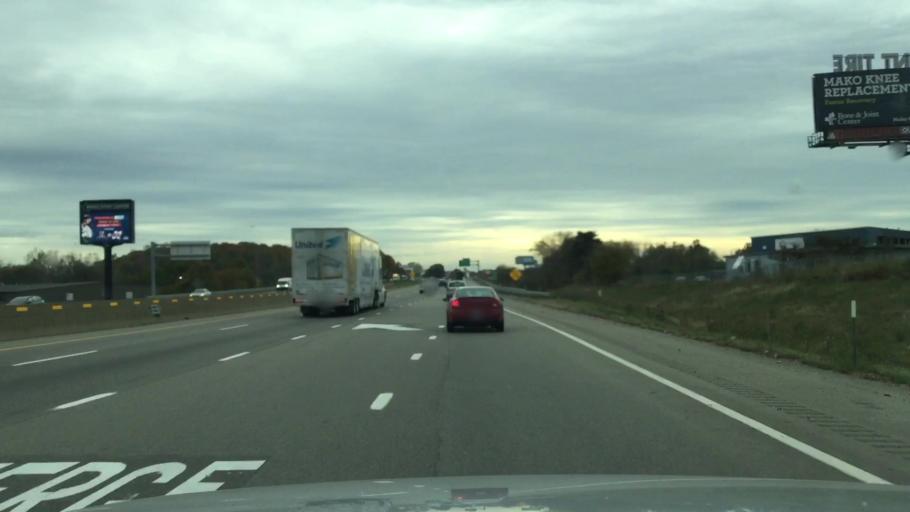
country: US
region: Michigan
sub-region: Kalamazoo County
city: Eastwood
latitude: 42.2567
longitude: -85.5349
